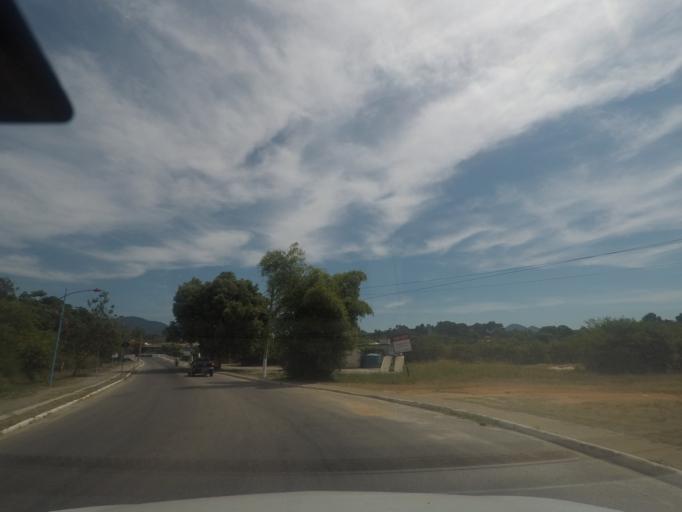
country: BR
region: Rio de Janeiro
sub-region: Marica
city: Marica
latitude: -22.9458
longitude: -42.7520
